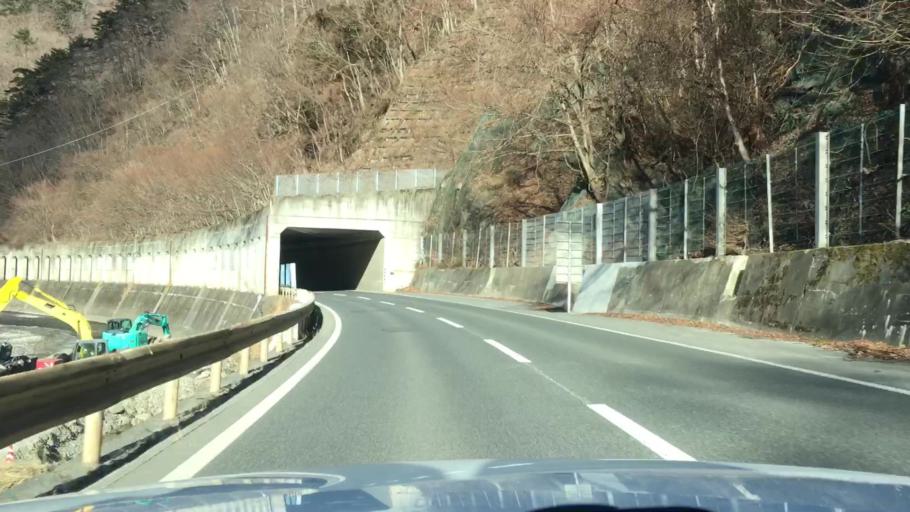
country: JP
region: Iwate
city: Miyako
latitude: 39.6044
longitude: 141.6533
